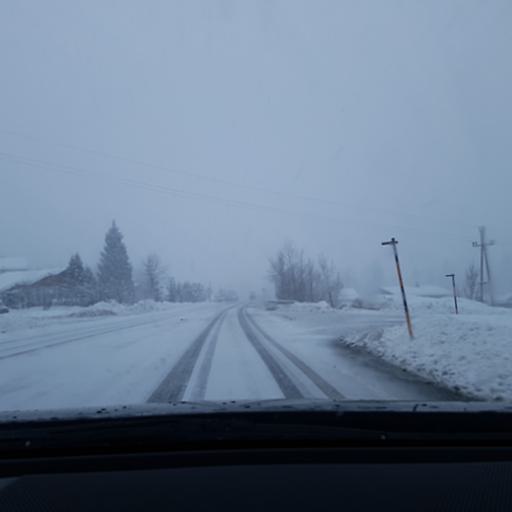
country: AT
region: Salzburg
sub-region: Politischer Bezirk Hallein
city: Abtenau
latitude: 47.5865
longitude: 13.4568
